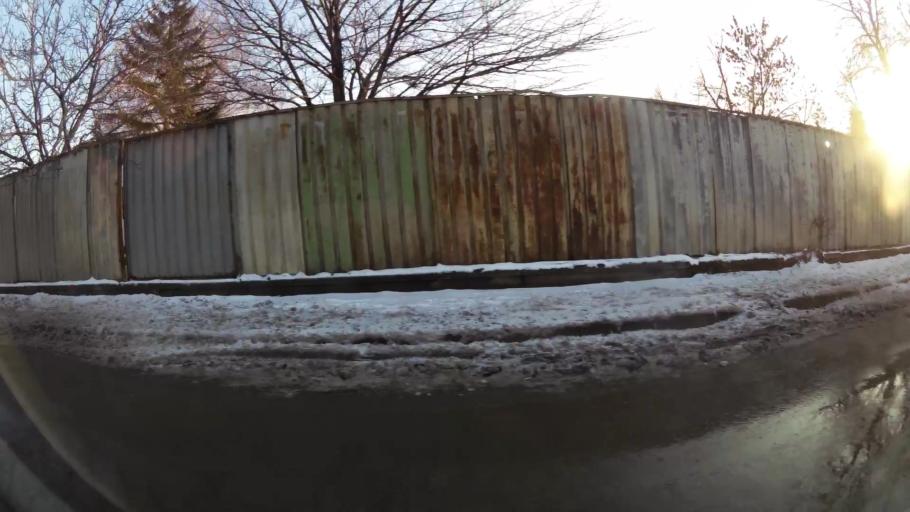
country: BG
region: Sofia-Capital
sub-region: Stolichna Obshtina
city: Sofia
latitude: 42.6759
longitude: 23.3804
